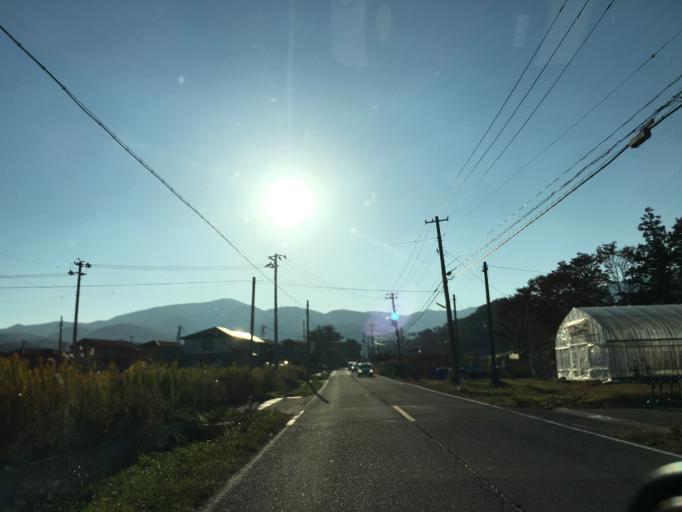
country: JP
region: Fukushima
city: Koriyama
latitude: 37.3963
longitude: 140.2475
